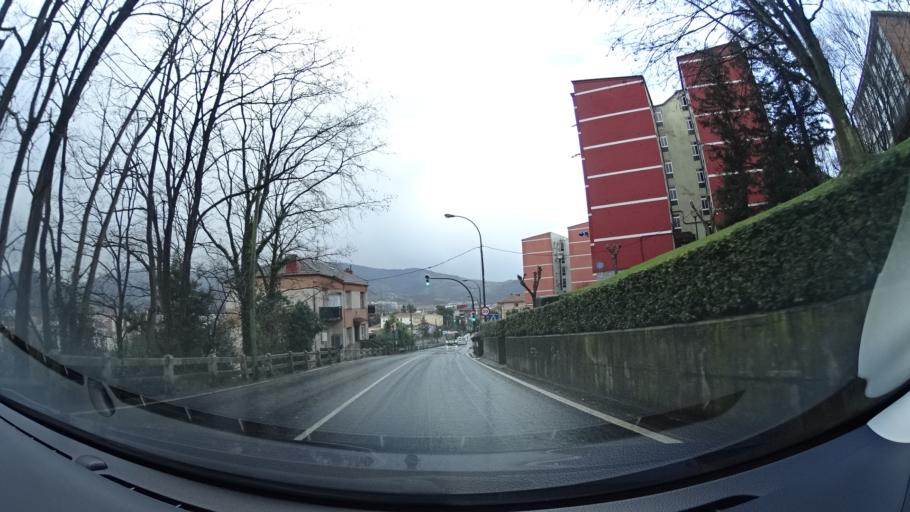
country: ES
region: Basque Country
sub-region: Bizkaia
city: Santutxu
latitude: 43.2626
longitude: -2.9082
